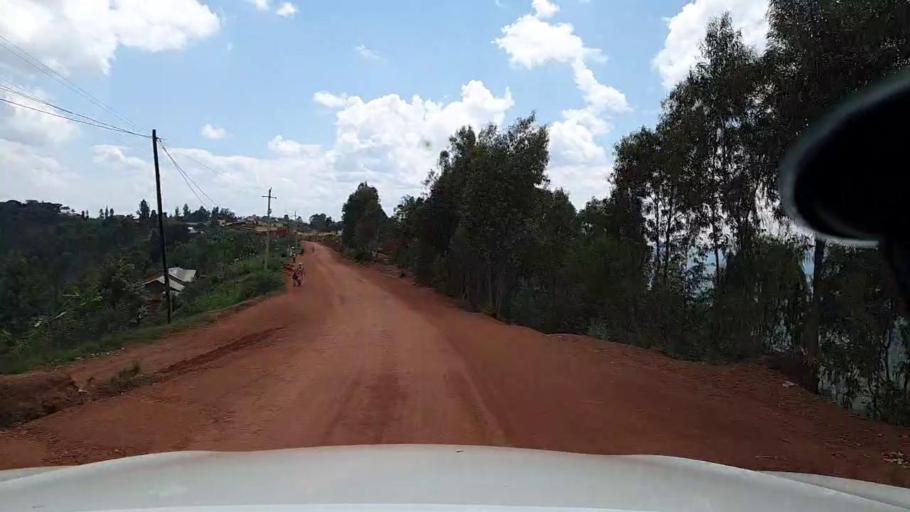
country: RW
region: Kigali
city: Kigali
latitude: -1.8016
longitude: 29.8429
